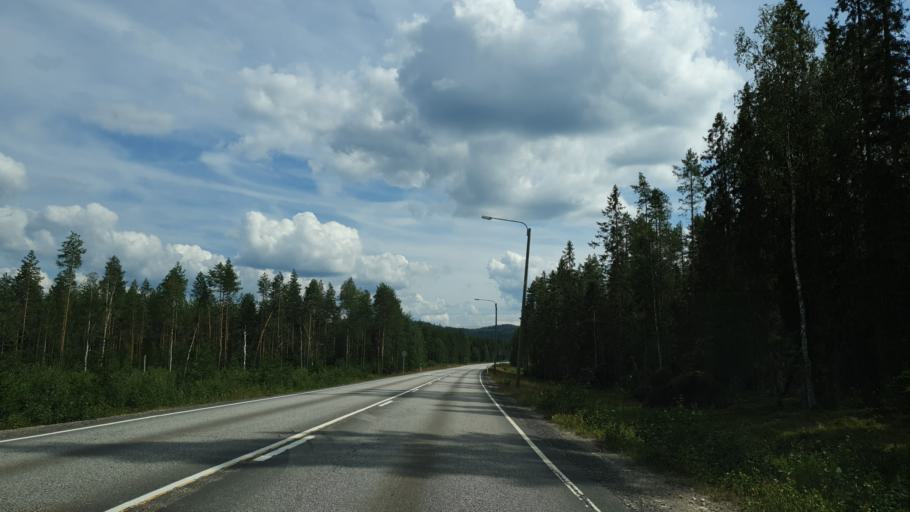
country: FI
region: Kainuu
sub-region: Kajaani
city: Vuokatti
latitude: 64.1150
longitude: 28.1771
